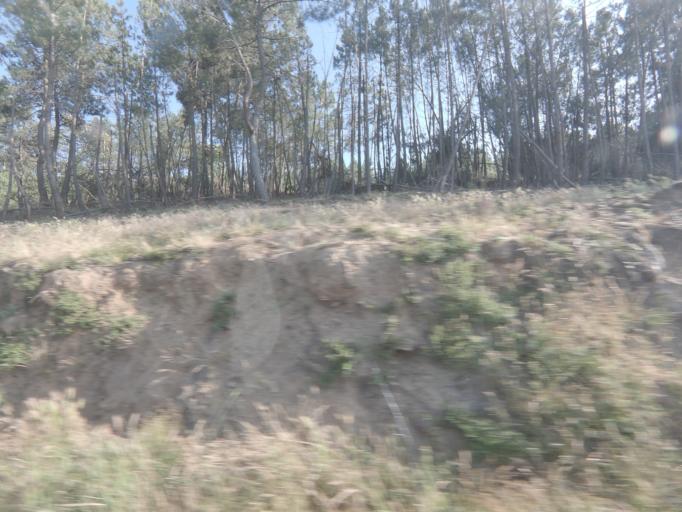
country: PT
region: Vila Real
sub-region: Sabrosa
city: Vilela
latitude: 41.1976
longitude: -7.6124
